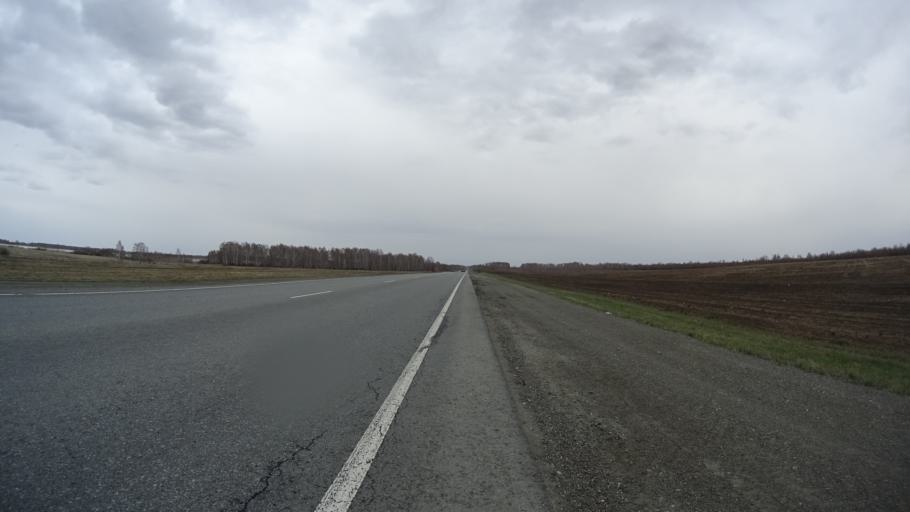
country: RU
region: Chelyabinsk
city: Krasnogorskiy
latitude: 54.6629
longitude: 61.2540
